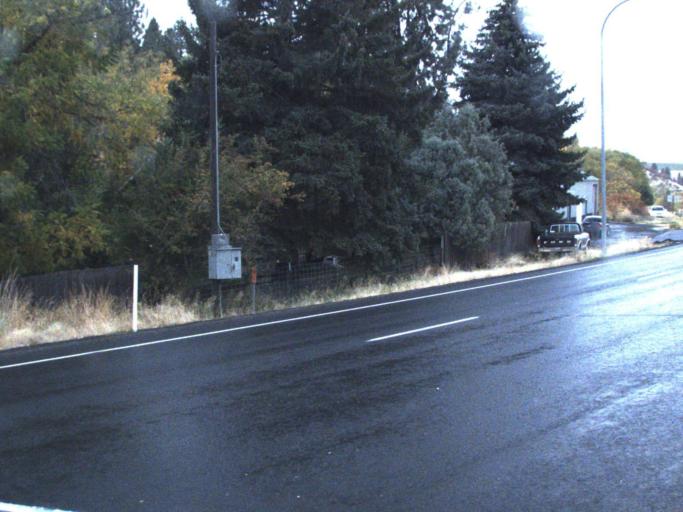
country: US
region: Washington
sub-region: Whitman County
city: Colfax
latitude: 46.8510
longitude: -117.3395
